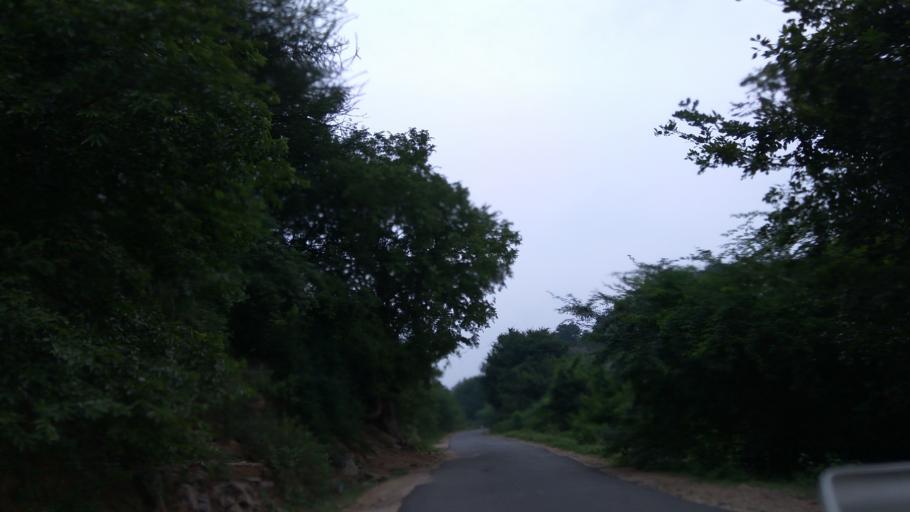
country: IN
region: Tamil Nadu
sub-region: Dharmapuri
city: Dharmapuri
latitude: 12.0141
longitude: 78.1287
